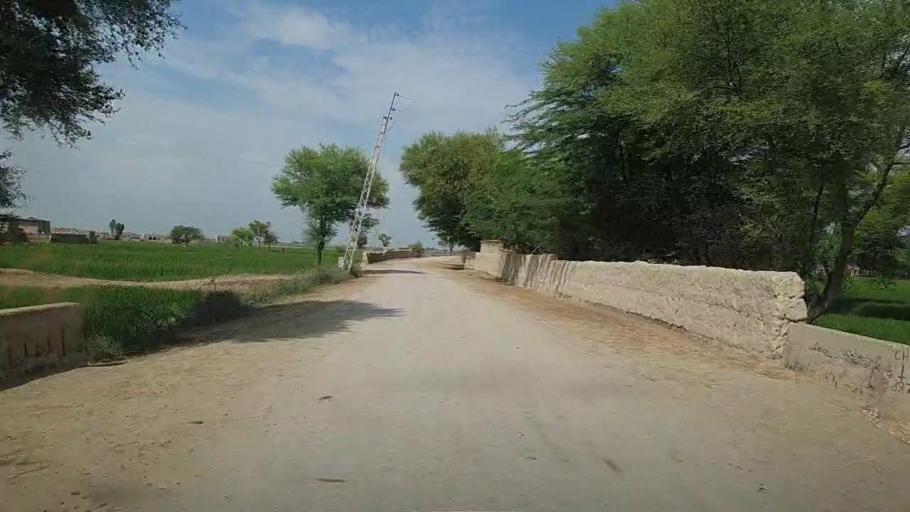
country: PK
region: Sindh
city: Thul
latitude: 28.2715
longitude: 68.8203
